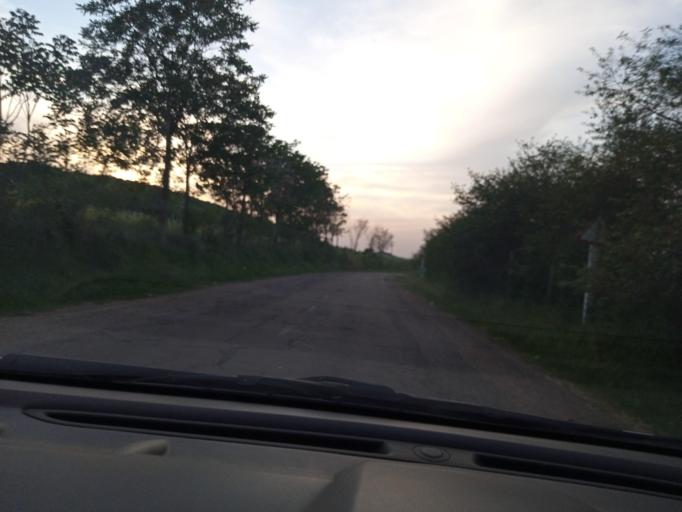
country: UZ
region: Toshkent
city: Parkent
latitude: 41.2371
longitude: 69.7355
